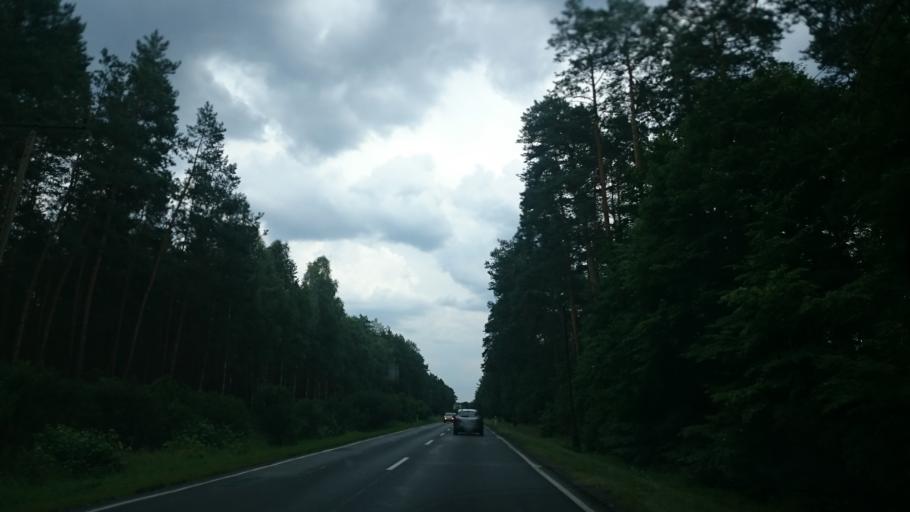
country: PL
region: Kujawsko-Pomorskie
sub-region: Powiat tucholski
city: Cekcyn
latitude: 53.5423
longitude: 17.9341
